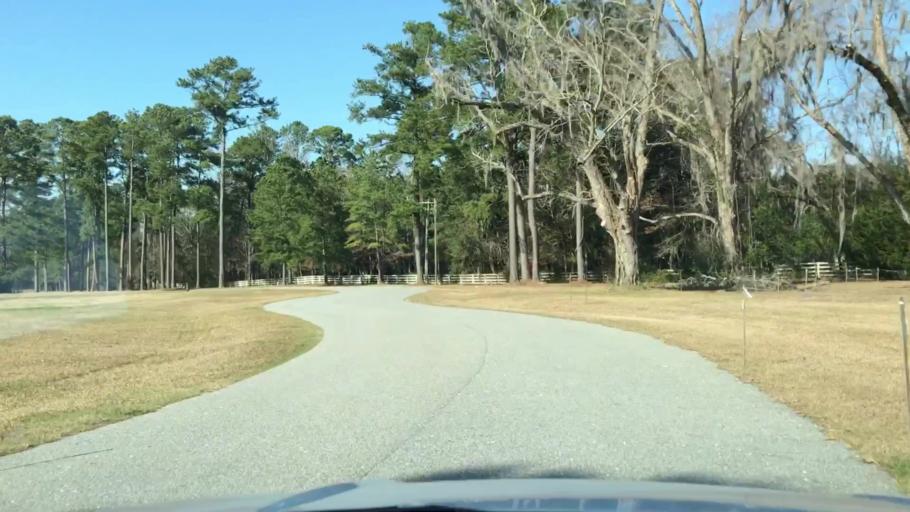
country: US
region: South Carolina
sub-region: Beaufort County
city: Bluffton
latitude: 32.3371
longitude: -80.9059
